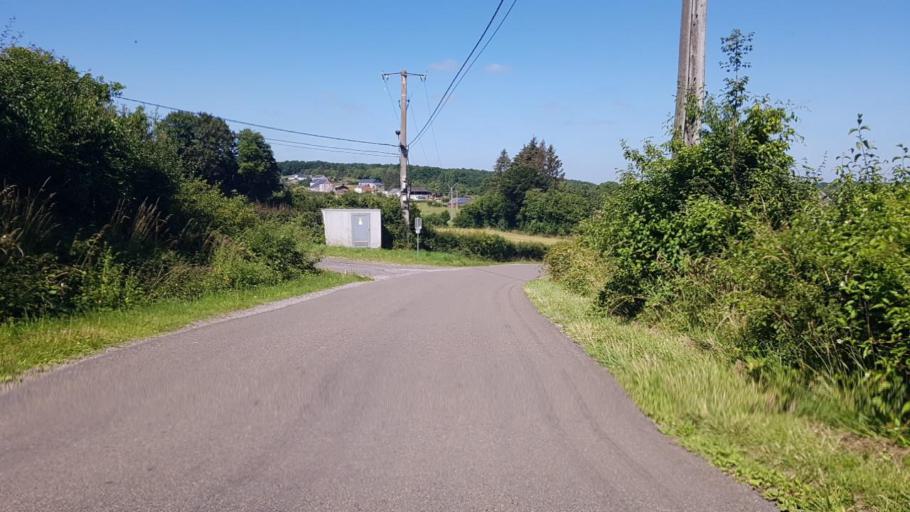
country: BE
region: Wallonia
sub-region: Province du Hainaut
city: Chimay
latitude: 50.0664
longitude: 4.2398
